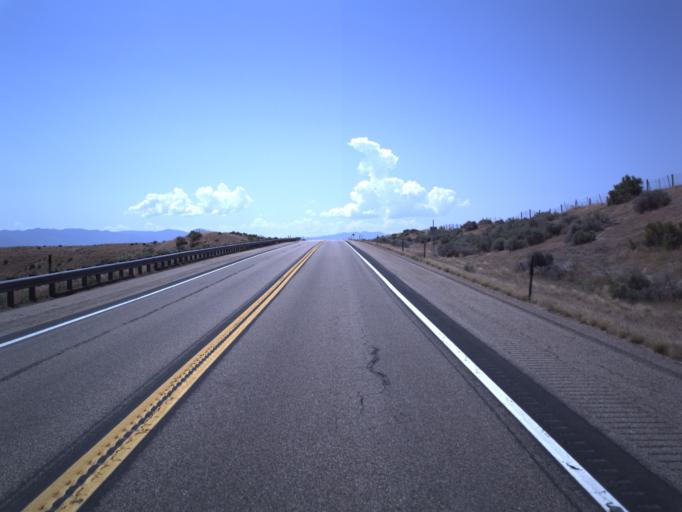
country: US
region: Utah
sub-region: Millard County
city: Delta
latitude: 39.3940
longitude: -112.5018
